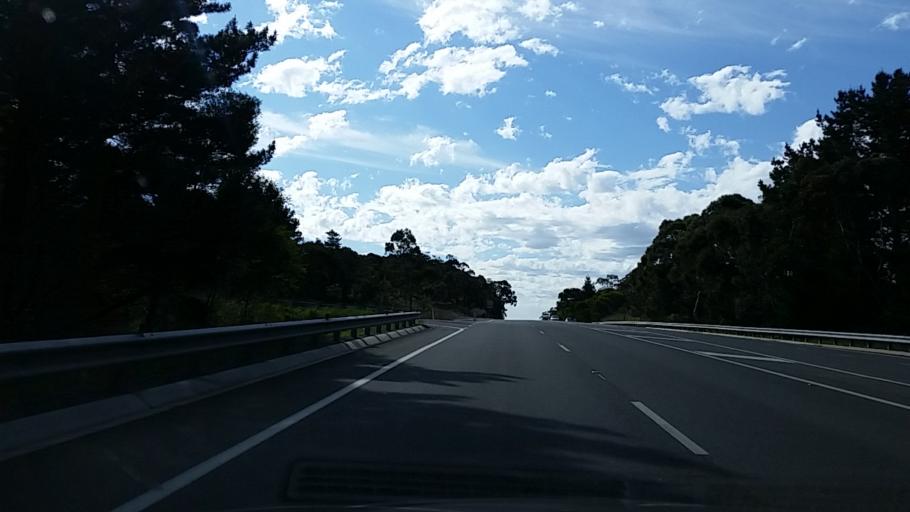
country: AU
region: South Australia
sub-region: Alexandrina
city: Mount Compass
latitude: -35.2946
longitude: 138.5795
